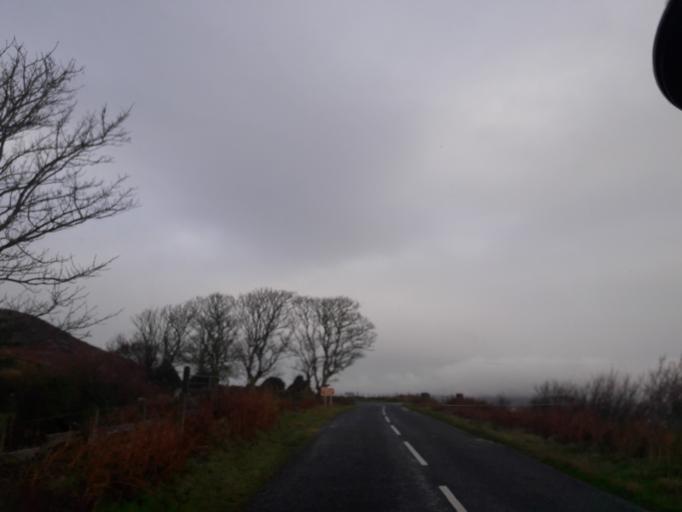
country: IE
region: Ulster
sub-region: County Donegal
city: Buncrana
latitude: 55.1768
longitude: -7.5784
